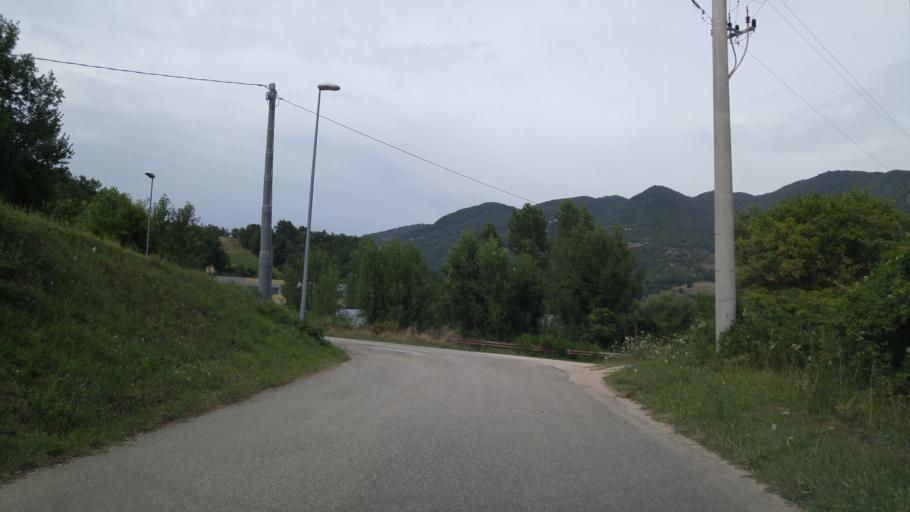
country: IT
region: The Marches
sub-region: Provincia di Pesaro e Urbino
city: Acqualagna
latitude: 43.6338
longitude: 12.6840
